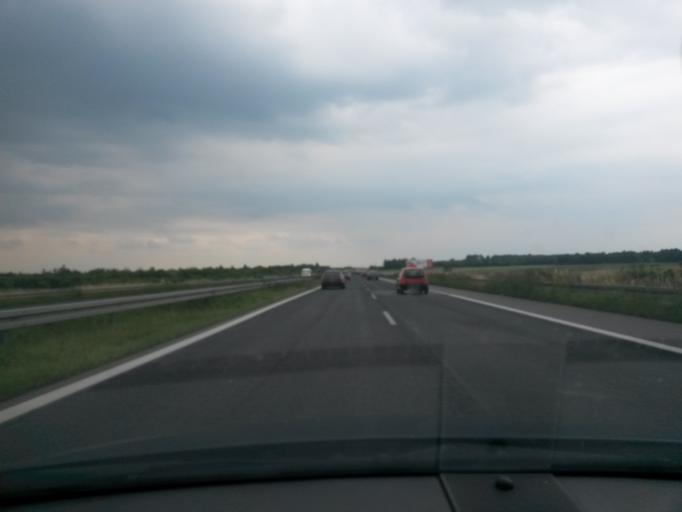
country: PL
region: Silesian Voivodeship
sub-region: Powiat czestochowski
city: Borowno
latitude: 50.9414
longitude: 19.2359
